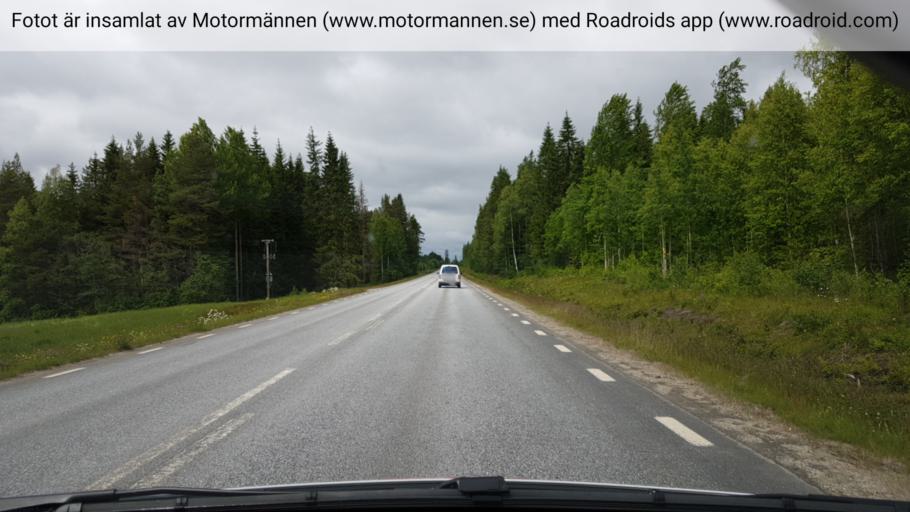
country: SE
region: Vaesterbotten
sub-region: Vannas Kommun
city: Vaennaes
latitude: 63.9736
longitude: 19.7352
